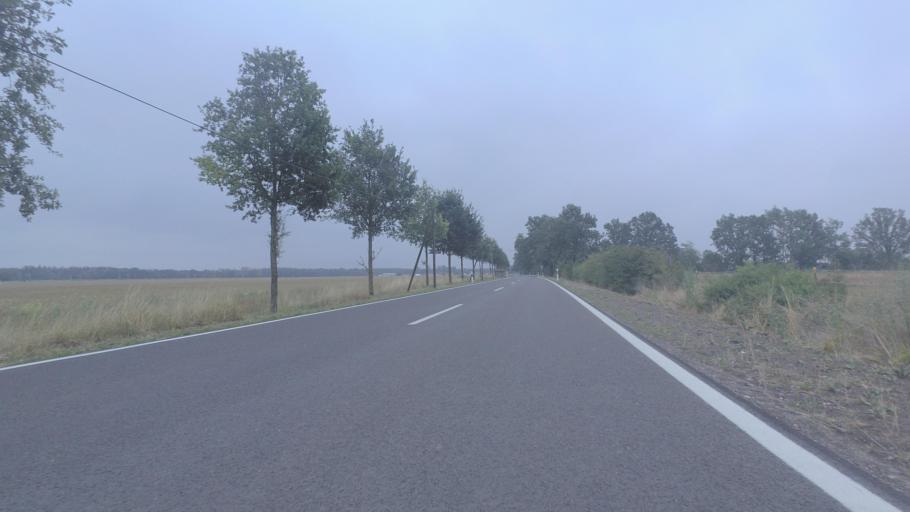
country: DE
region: Brandenburg
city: Paulinenaue
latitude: 52.6601
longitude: 12.7405
